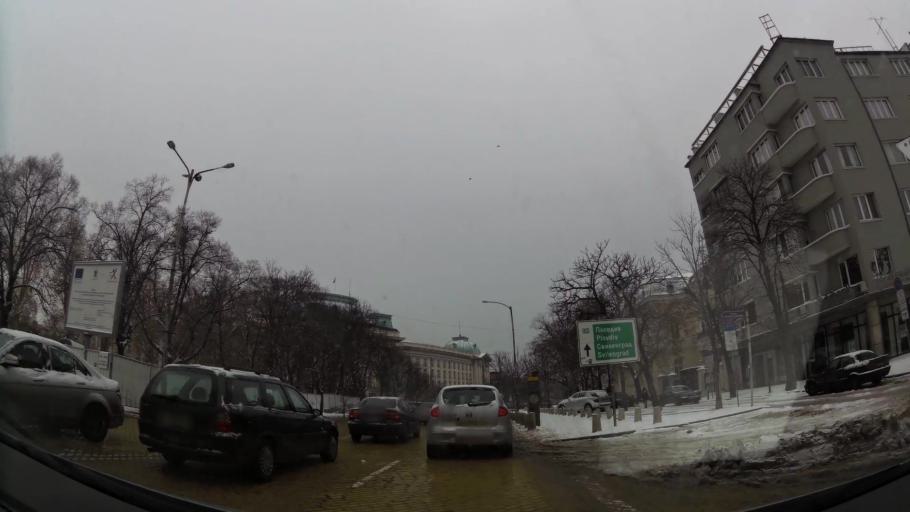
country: BG
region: Sofia-Capital
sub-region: Stolichna Obshtina
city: Sofia
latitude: 42.6937
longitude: 23.3329
